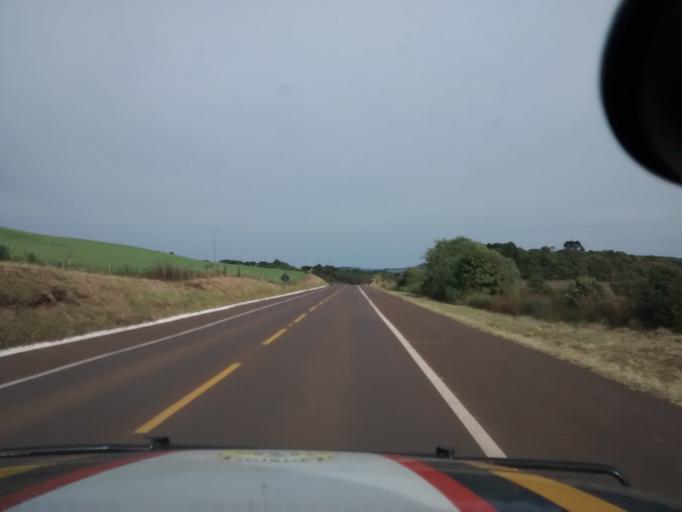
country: BR
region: Rio Grande do Sul
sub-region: Lagoa Vermelha
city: Lagoa Vermelha
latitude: -28.3353
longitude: -51.3018
